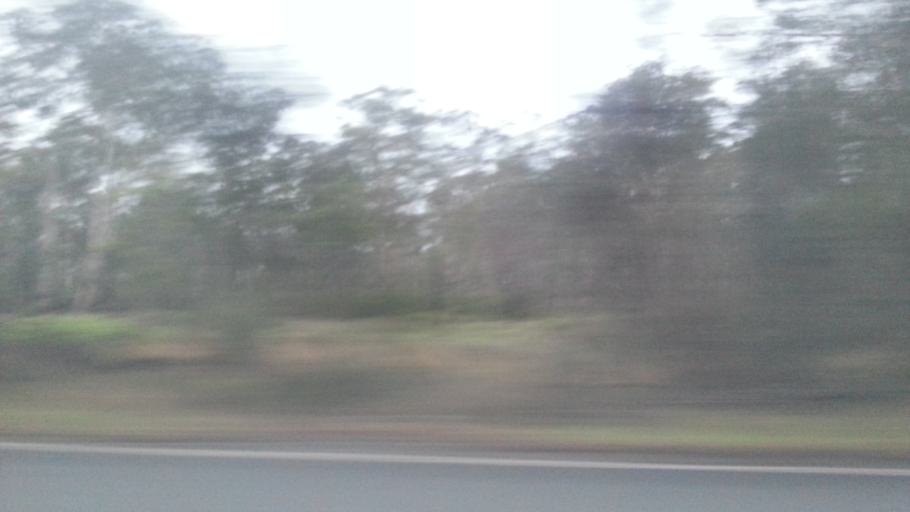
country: AU
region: New South Wales
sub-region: Wollondilly
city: Douglas Park
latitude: -34.2182
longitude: 150.7237
